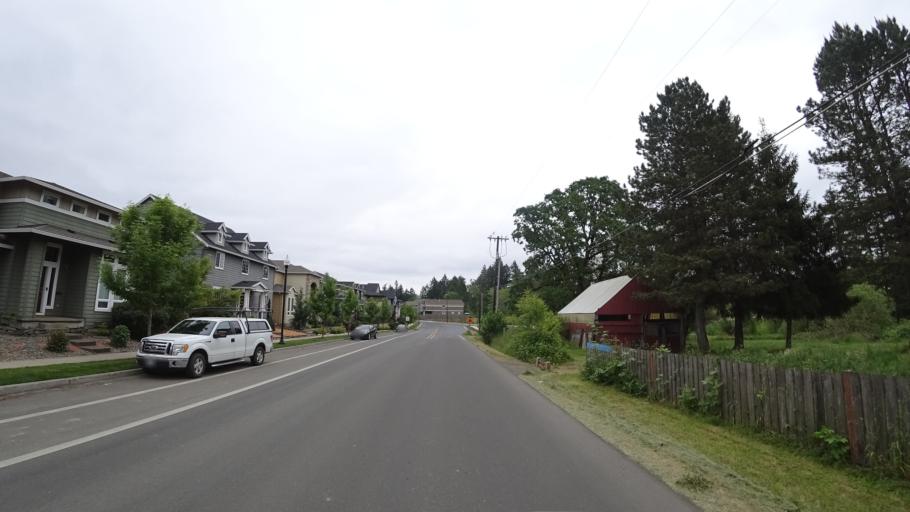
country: US
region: Oregon
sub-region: Washington County
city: Aloha
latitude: 45.4941
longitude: -122.9209
